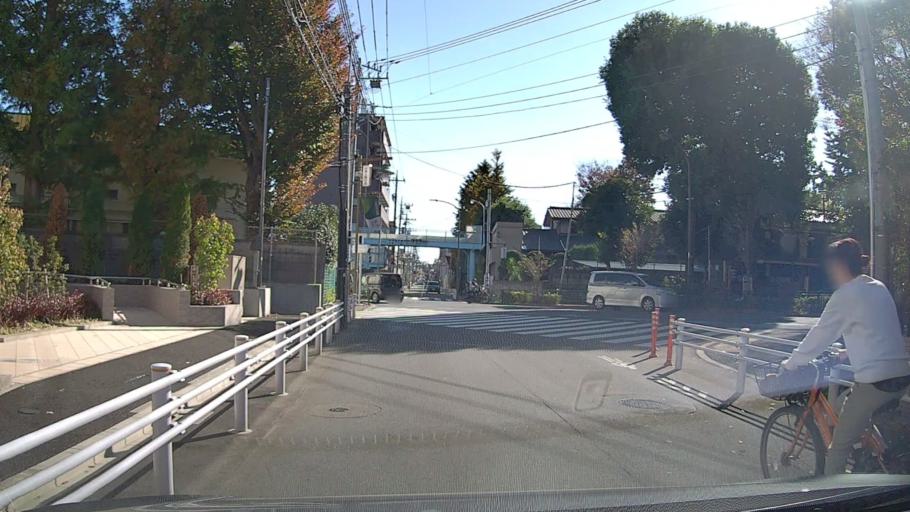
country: JP
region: Saitama
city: Wako
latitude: 35.7280
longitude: 139.6188
